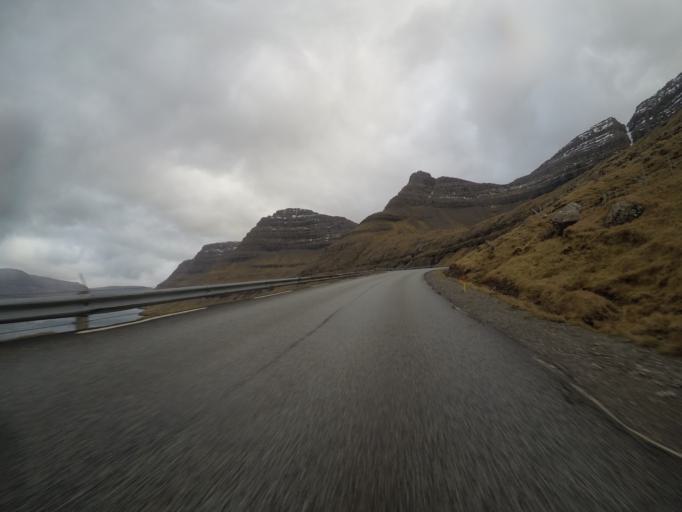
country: FO
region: Nordoyar
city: Klaksvik
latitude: 62.2793
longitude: -6.5234
